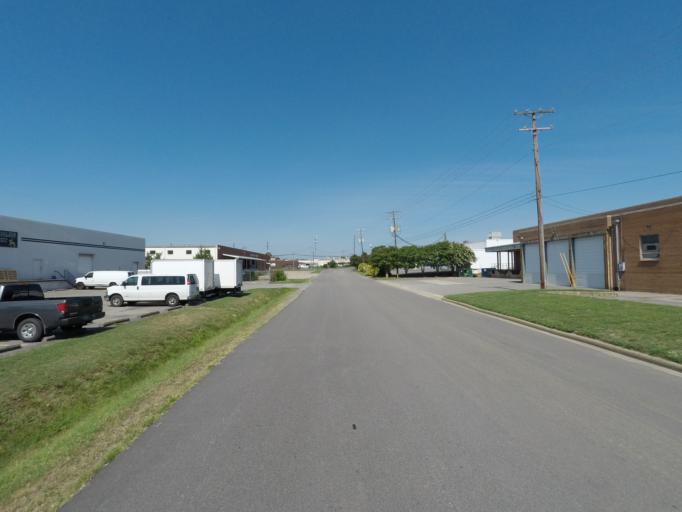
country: US
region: Virginia
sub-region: Henrico County
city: Dumbarton
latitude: 37.5788
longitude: -77.4802
